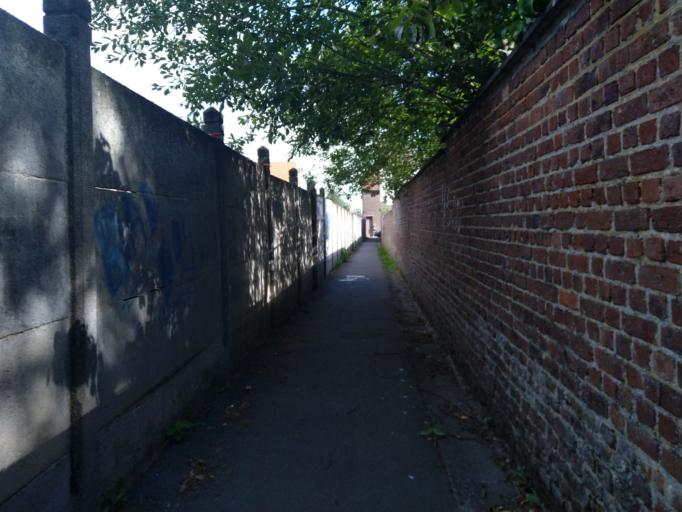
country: BE
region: Wallonia
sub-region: Province du Hainaut
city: Boussu
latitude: 50.4342
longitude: 3.7983
